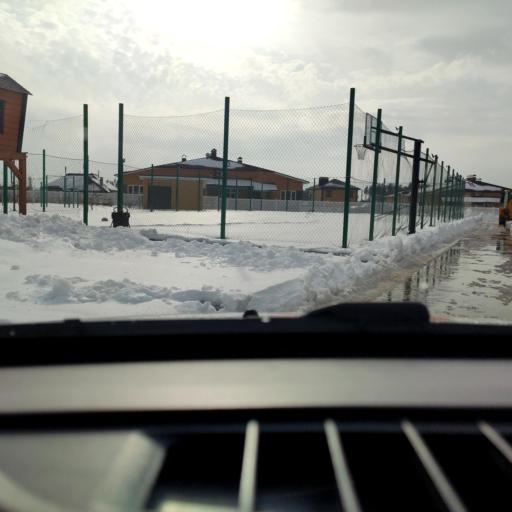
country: RU
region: Voronezj
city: Podgornoye
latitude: 51.7707
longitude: 39.1270
